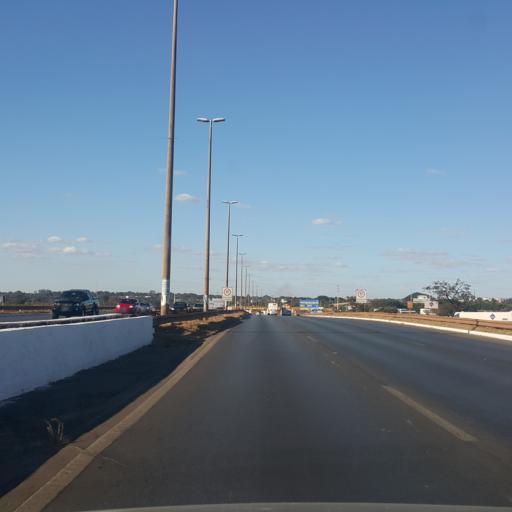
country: BR
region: Federal District
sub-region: Brasilia
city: Brasilia
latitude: -15.7899
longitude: -47.9503
